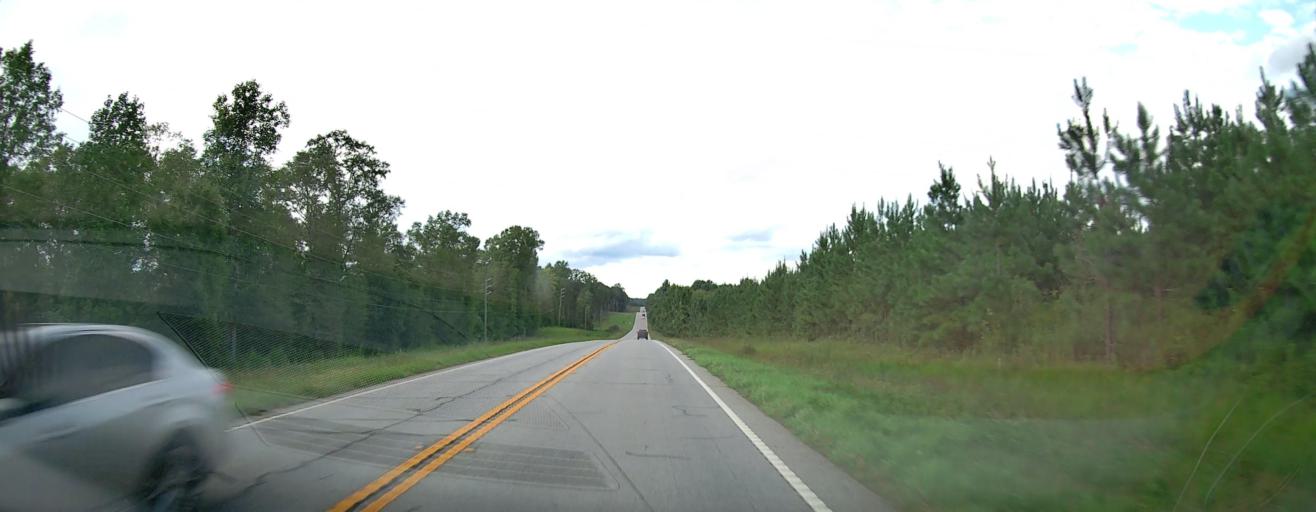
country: US
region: Georgia
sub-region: Meriwether County
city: Greenville
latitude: 33.0499
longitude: -84.5678
